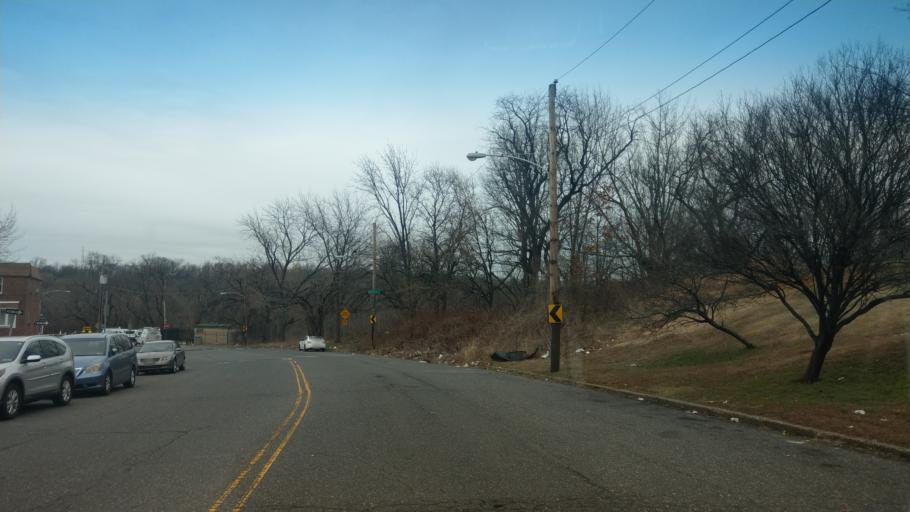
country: US
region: Pennsylvania
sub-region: Montgomery County
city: Rockledge
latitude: 40.0153
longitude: -75.1072
